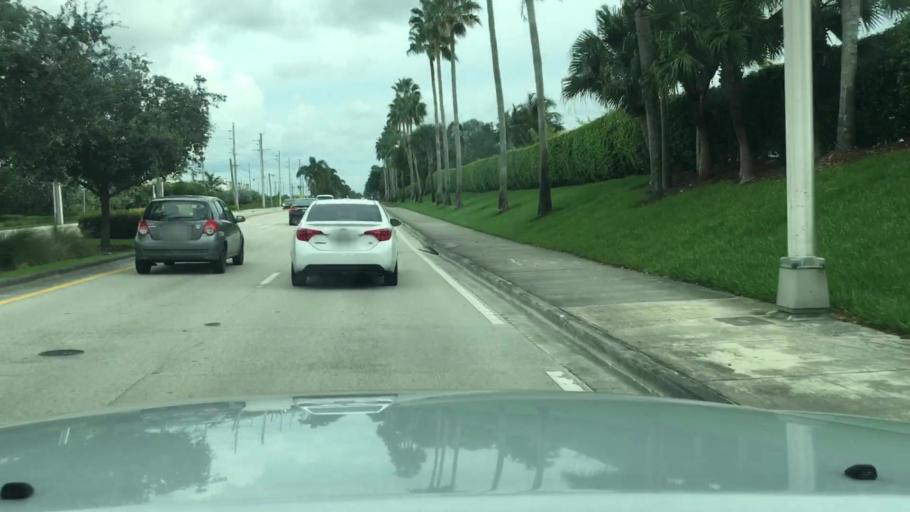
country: US
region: Florida
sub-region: Miami-Dade County
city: Doral
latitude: 25.8381
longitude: -80.3704
